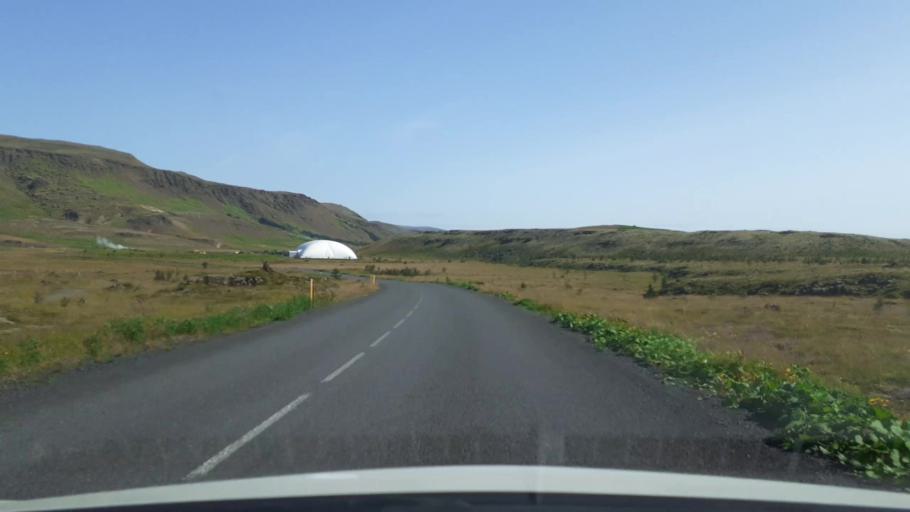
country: IS
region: South
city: Hveragerdi
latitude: 64.0142
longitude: -21.2080
